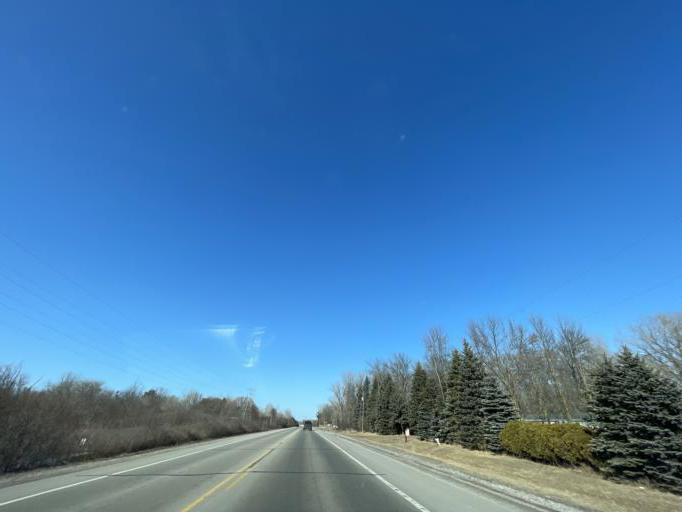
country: US
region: Wisconsin
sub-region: Brown County
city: Howard
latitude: 44.5942
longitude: -88.0779
